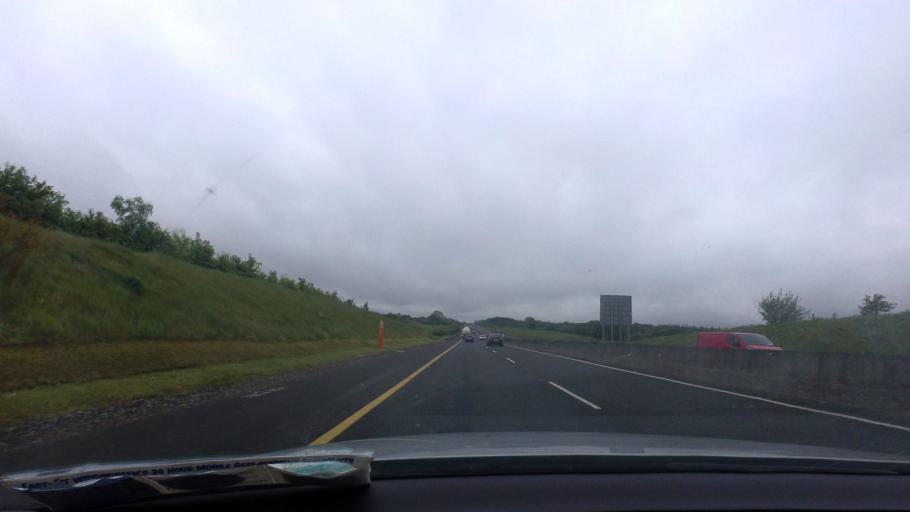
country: IE
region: Munster
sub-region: North Tipperary
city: Newport
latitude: 52.7429
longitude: -8.4386
